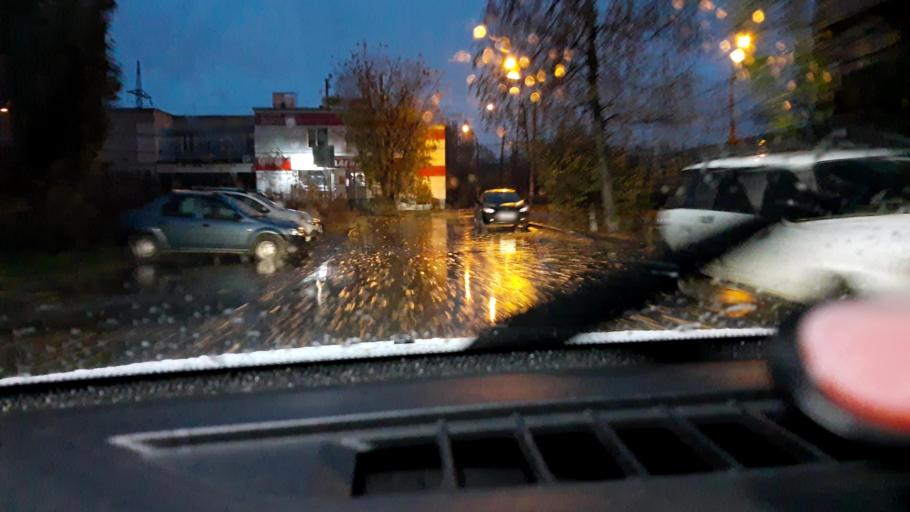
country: RU
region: Nizjnij Novgorod
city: Nizhniy Novgorod
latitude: 56.3160
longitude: 43.8781
